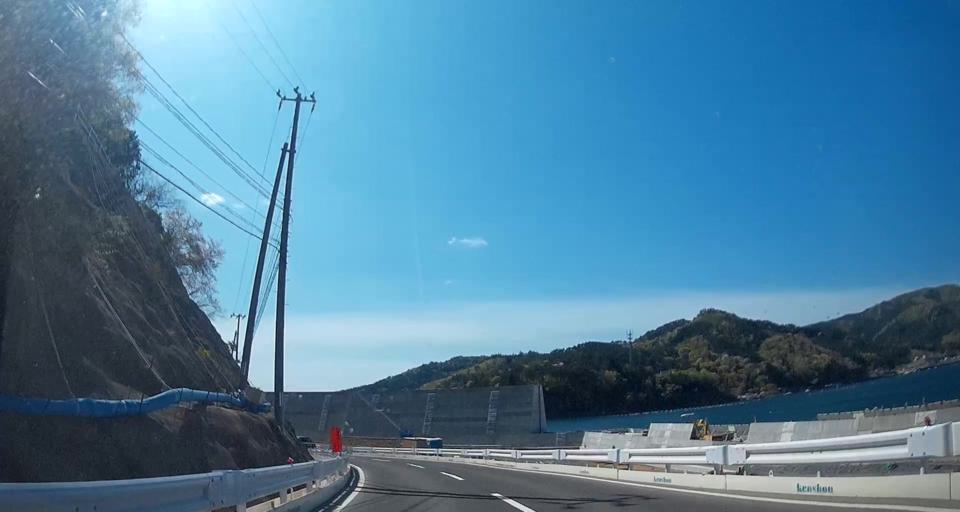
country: JP
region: Miyagi
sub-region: Oshika Gun
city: Onagawa Cho
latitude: 38.5215
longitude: 141.4715
